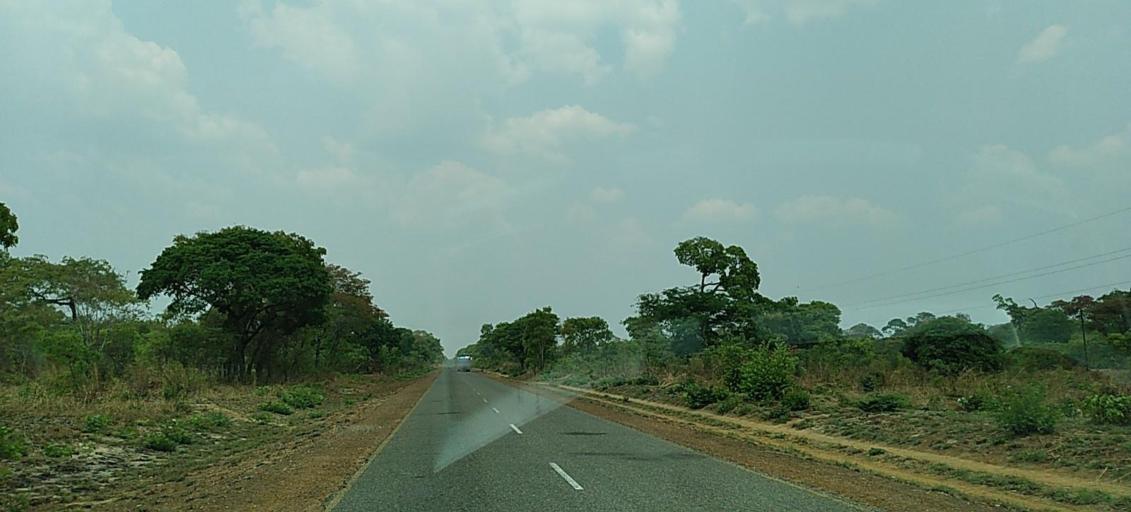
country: ZM
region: North-Western
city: Zambezi
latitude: -13.5559
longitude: 23.1806
